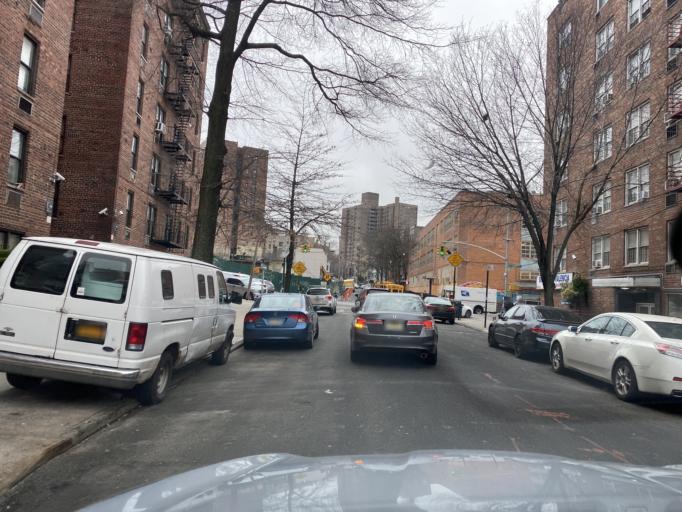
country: US
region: New York
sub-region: New York County
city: Inwood
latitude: 40.8731
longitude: -73.9043
